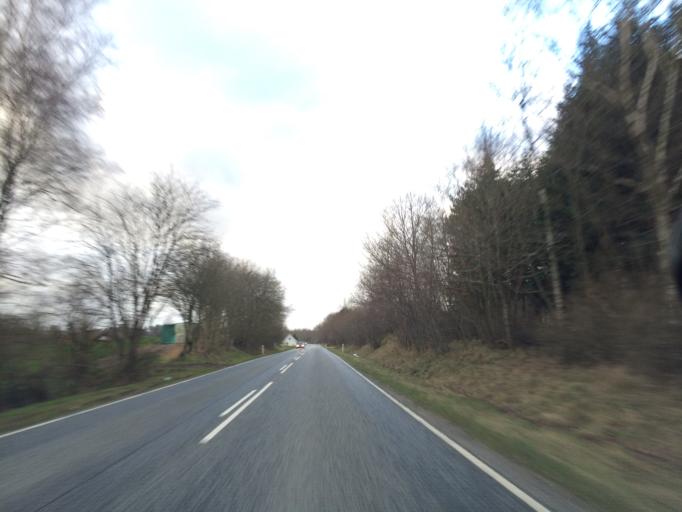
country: DK
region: Central Jutland
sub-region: Silkeborg Kommune
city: Svejbaek
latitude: 56.1028
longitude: 9.5949
